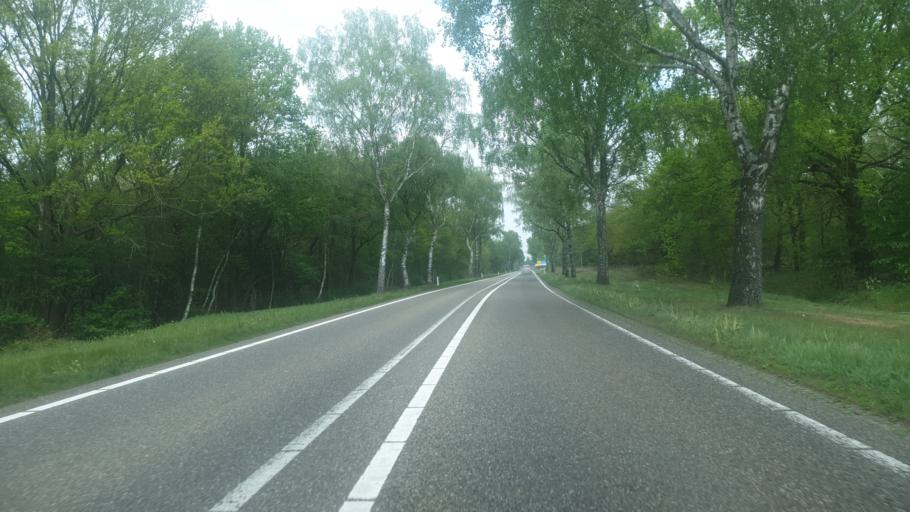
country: NL
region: North Brabant
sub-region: Gemeente Landerd
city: Reek
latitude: 51.7293
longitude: 5.6689
